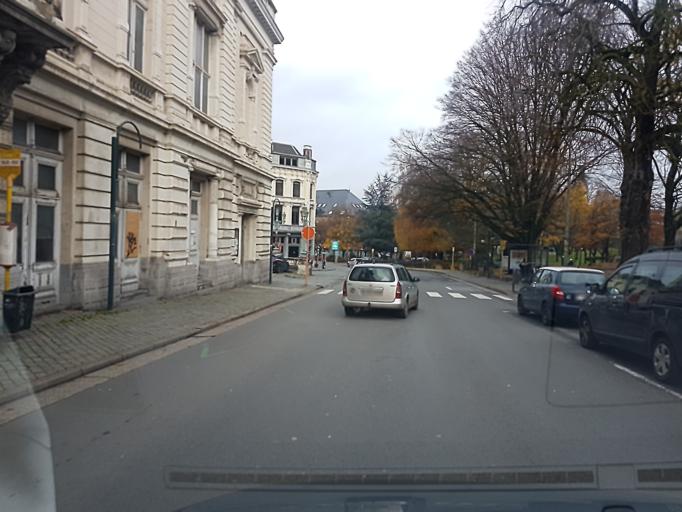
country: BE
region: Wallonia
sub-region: Province de Liege
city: Verviers
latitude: 50.5900
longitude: 5.8572
